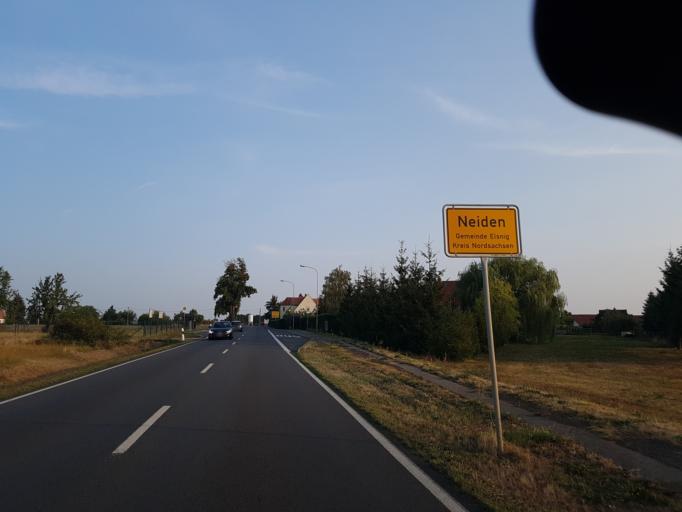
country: DE
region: Saxony
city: Elsnig
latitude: 51.5951
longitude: 12.9472
